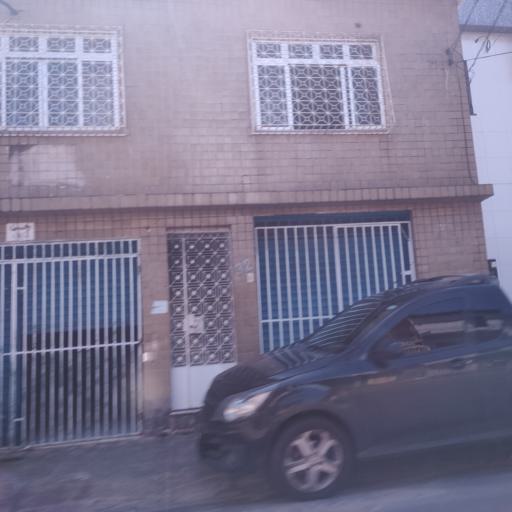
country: BR
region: Maranhao
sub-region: Sao Luis
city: Sao Luis
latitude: -2.5404
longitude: -44.2794
